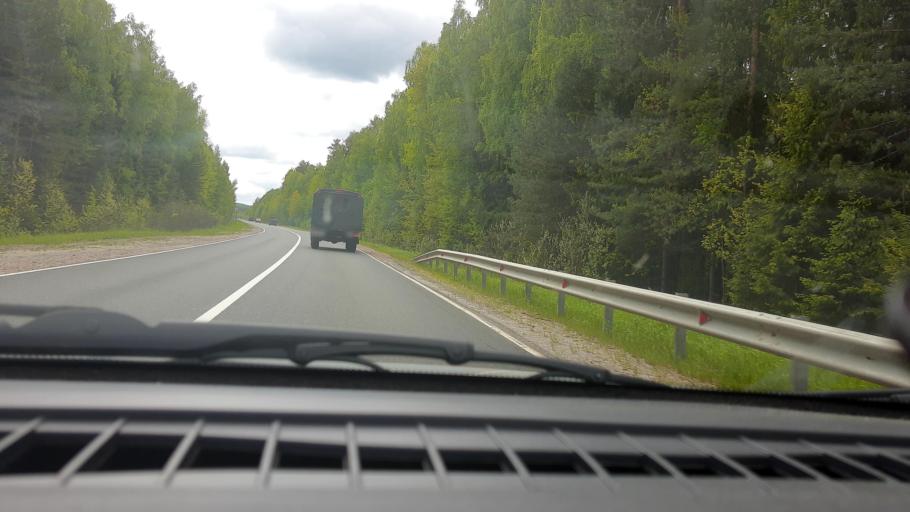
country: RU
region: Nizjnij Novgorod
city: Krasnyye Baki
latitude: 57.1312
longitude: 45.2132
